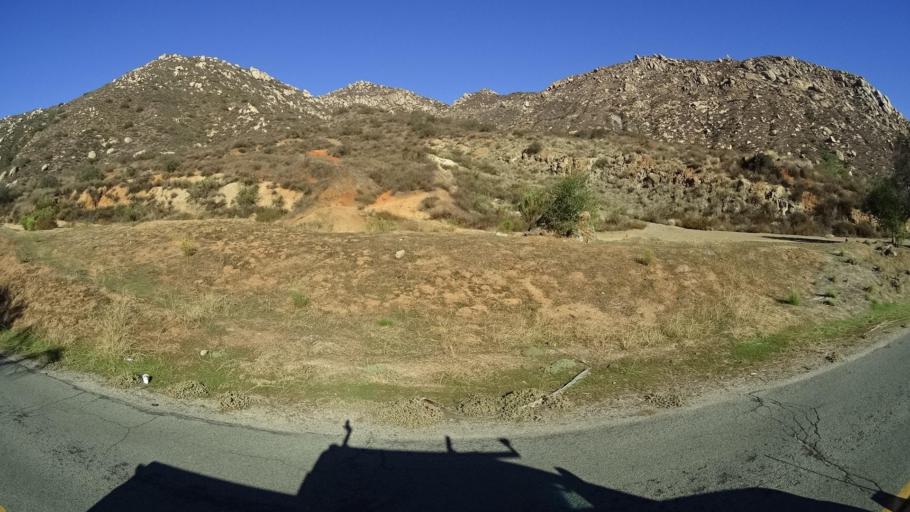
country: MX
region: Baja California
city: Tecate
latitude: 32.6204
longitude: -116.6935
